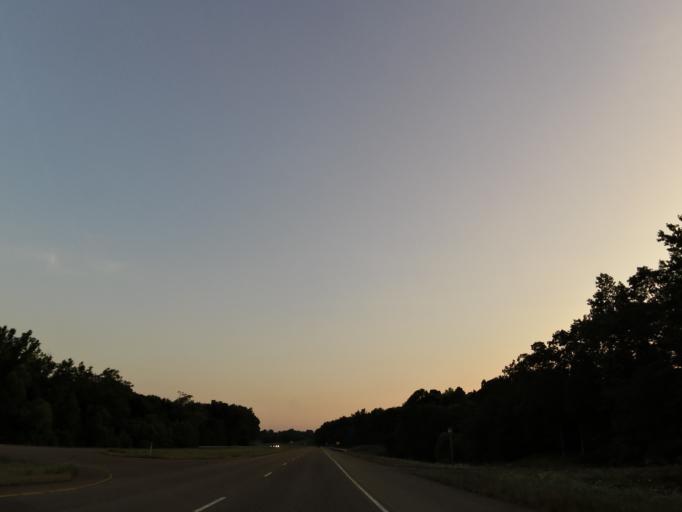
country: US
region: Tennessee
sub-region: Henry County
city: Paris
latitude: 36.2085
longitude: -88.4019
